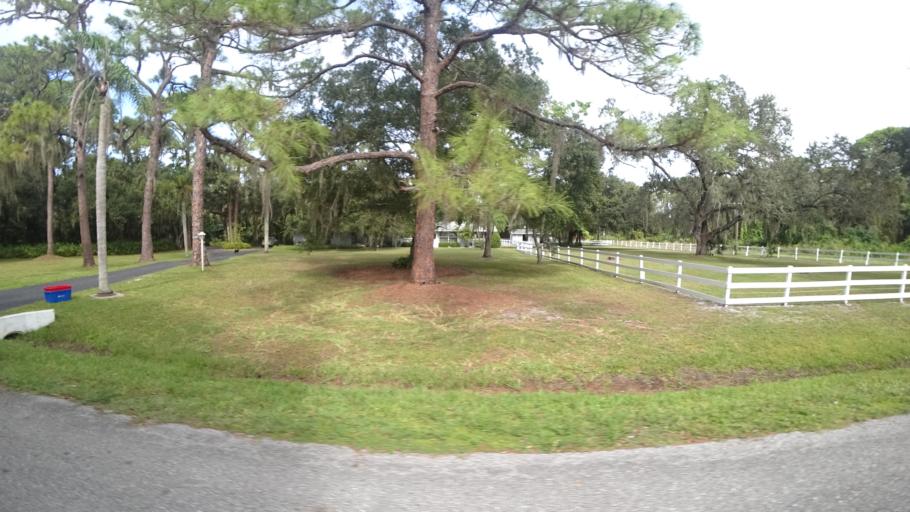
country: US
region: Florida
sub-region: Sarasota County
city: North Sarasota
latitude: 27.3870
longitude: -82.5288
